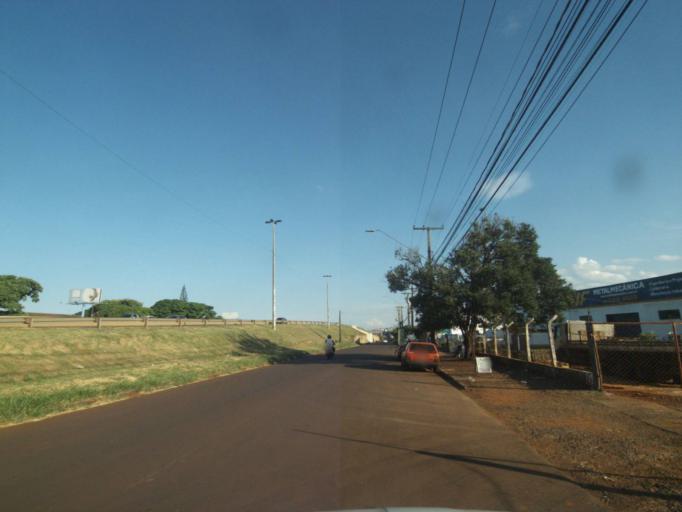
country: BR
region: Parana
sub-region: Cambe
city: Cambe
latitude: -23.3033
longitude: -51.2251
